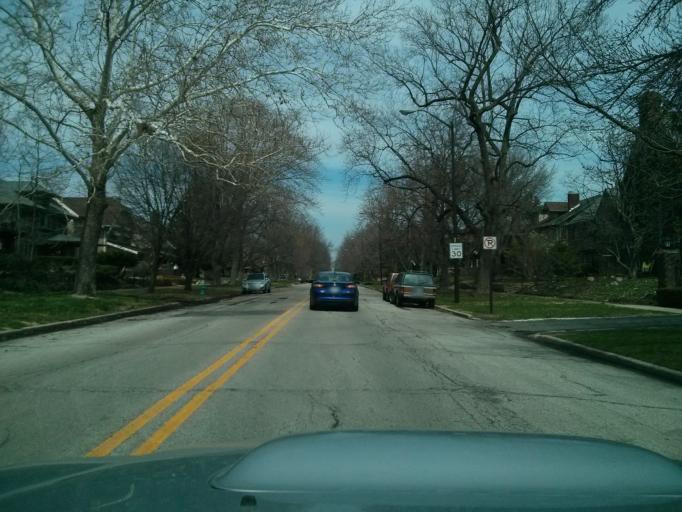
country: US
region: Indiana
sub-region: Marion County
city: Broad Ripple
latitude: 39.8253
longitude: -86.1521
